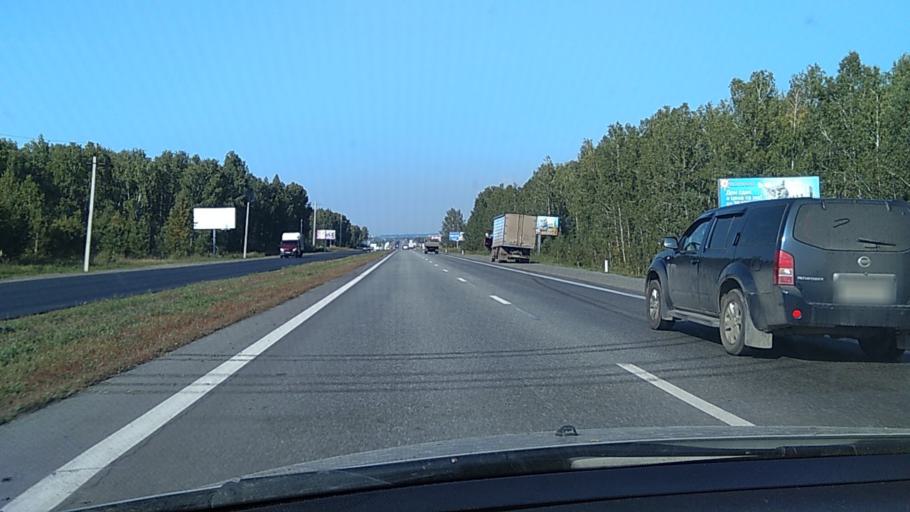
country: RU
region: Chelyabinsk
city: Sargazy
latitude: 55.0292
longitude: 61.2973
